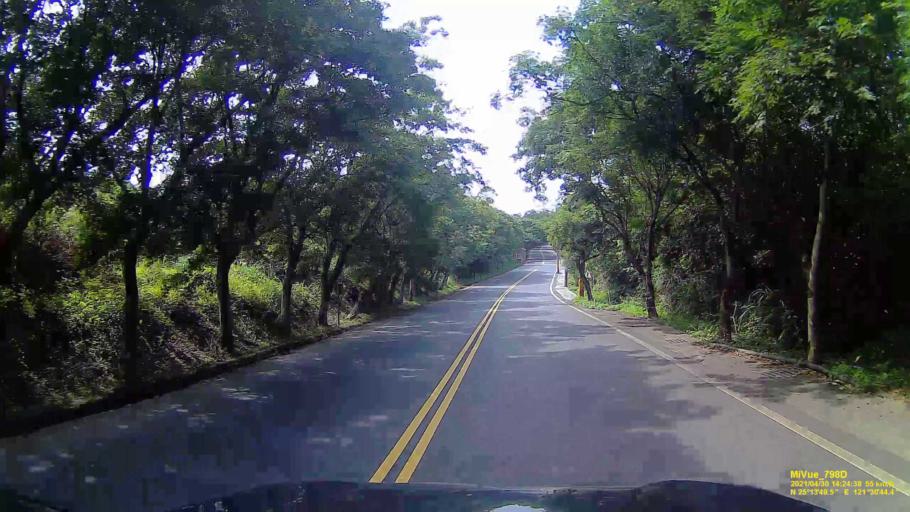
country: TW
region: Taipei
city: Taipei
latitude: 25.2307
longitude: 121.5121
